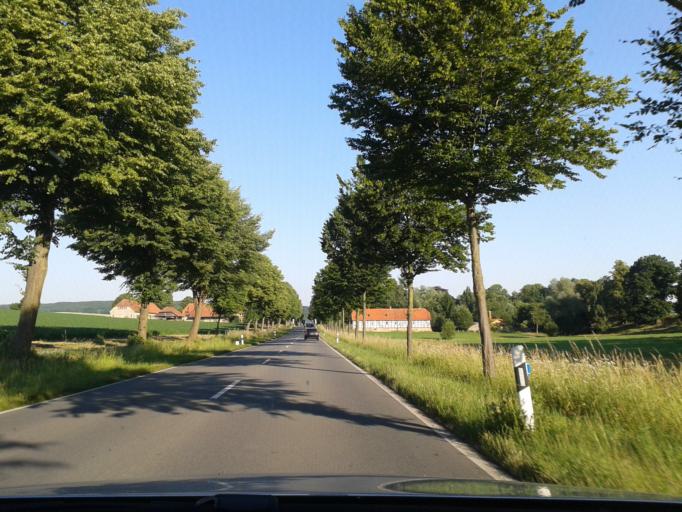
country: DE
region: North Rhine-Westphalia
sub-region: Regierungsbezirk Detmold
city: Barntrup
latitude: 51.9965
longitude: 9.0902
